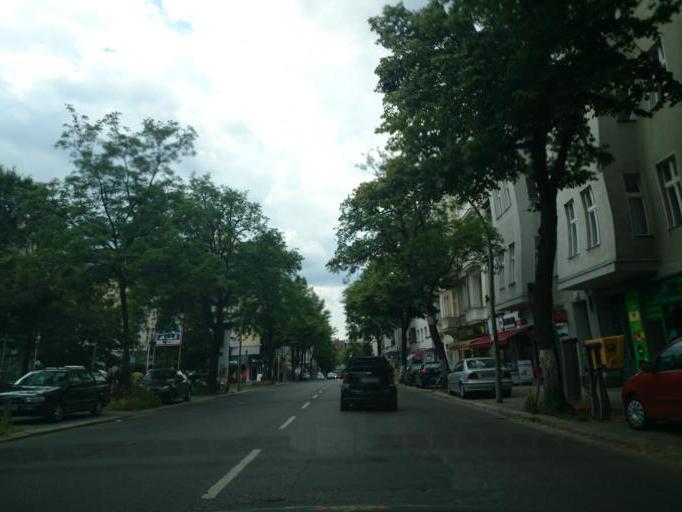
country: DE
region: Berlin
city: Steglitz Bezirk
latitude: 52.4548
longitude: 13.3273
